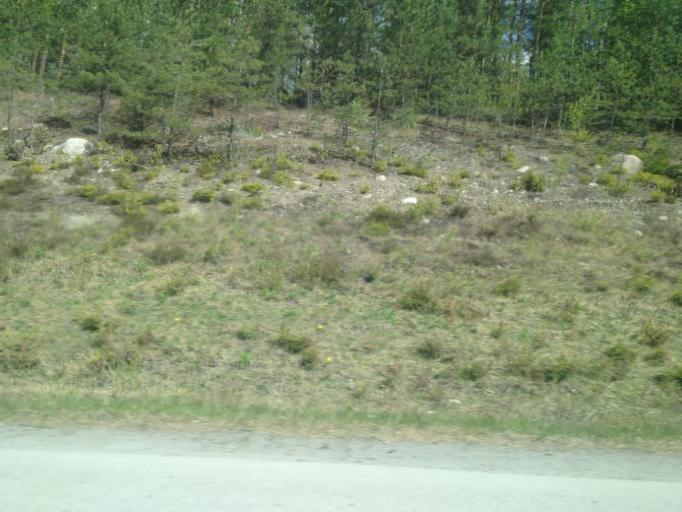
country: FI
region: Haeme
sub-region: Haemeenlinna
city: Janakkala
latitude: 60.9190
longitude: 24.5317
